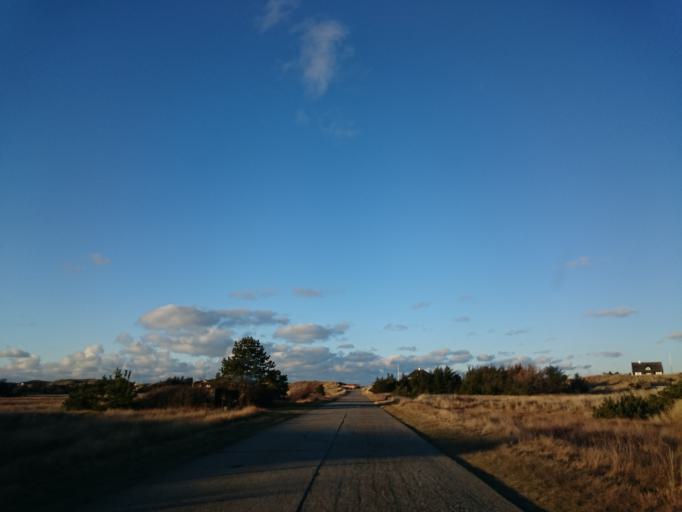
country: DK
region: North Denmark
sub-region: Frederikshavn Kommune
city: Skagen
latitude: 57.7222
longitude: 10.5303
